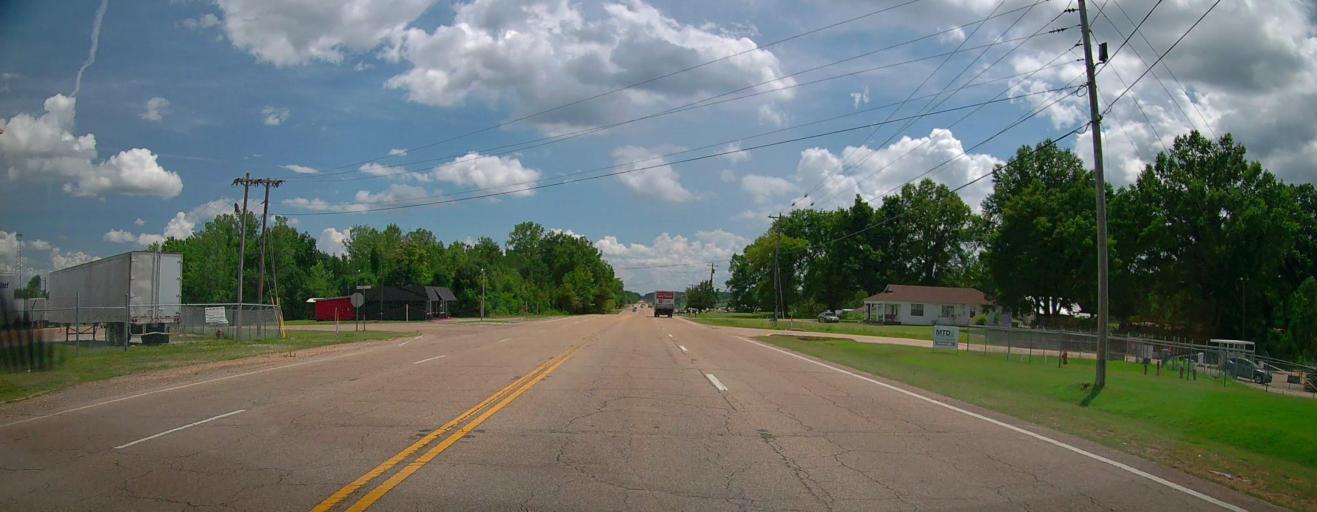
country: US
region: Mississippi
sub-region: Lee County
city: Verona
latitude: 34.1597
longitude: -88.7195
